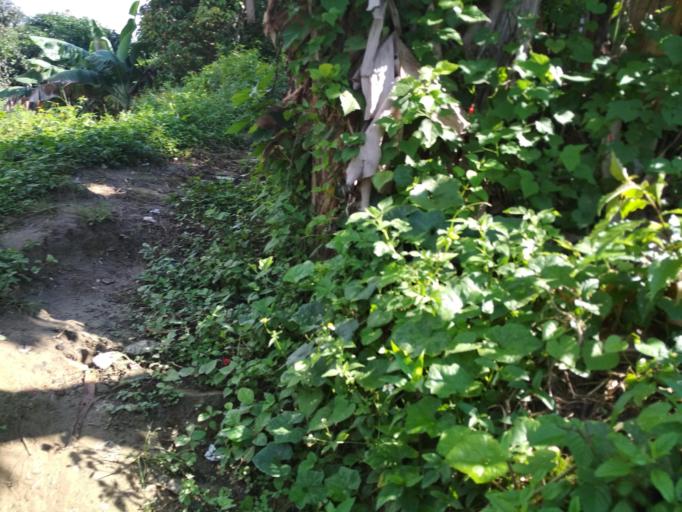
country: MX
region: Veracruz
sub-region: San Andres Tuxtla
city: Texcaltitan Xoteapan (Texcaltitan)
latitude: 18.4486
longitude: -95.2521
